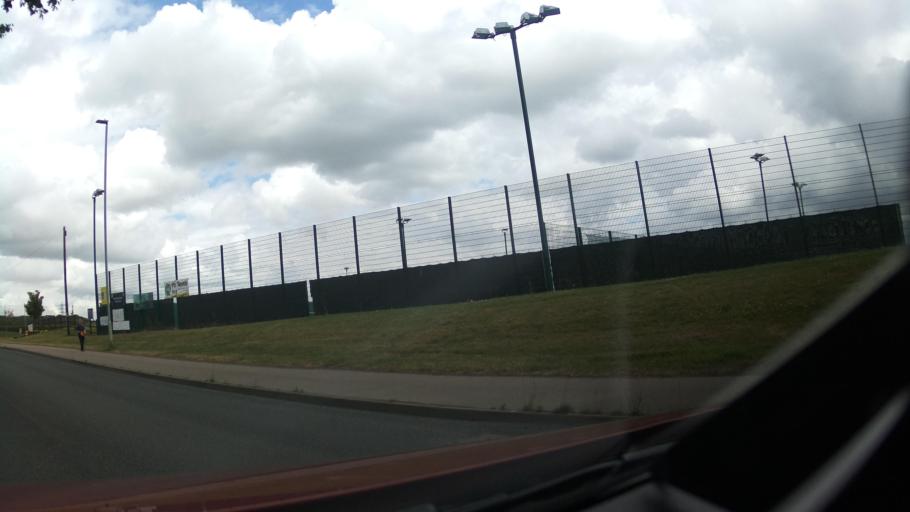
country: GB
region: England
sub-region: Wiltshire
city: Royal Wootton Bassett
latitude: 51.5537
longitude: -1.8979
